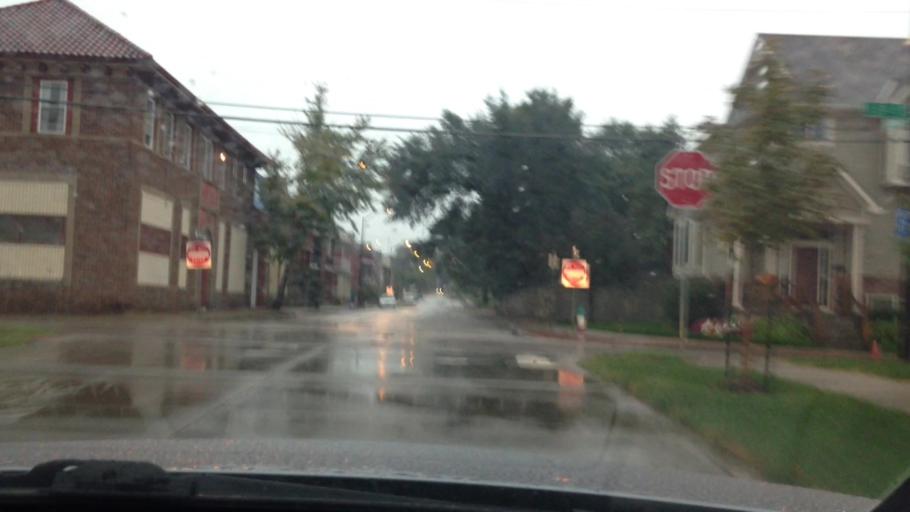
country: US
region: Missouri
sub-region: Jackson County
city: Kansas City
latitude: 39.1102
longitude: -94.5747
